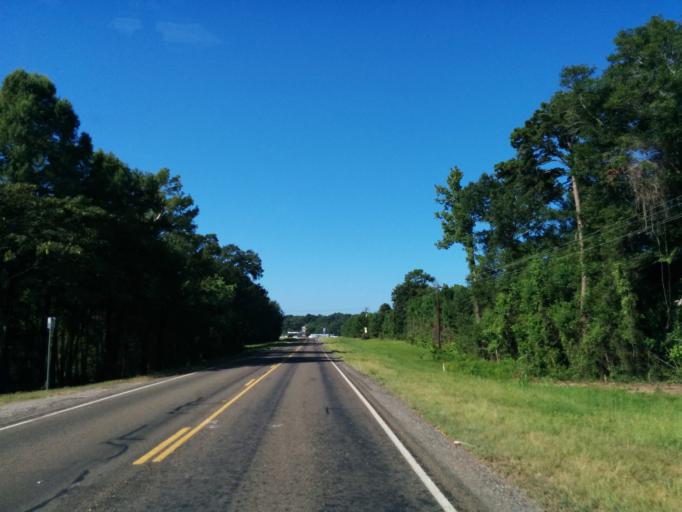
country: US
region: Texas
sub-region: Sabine County
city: Milam
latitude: 31.4533
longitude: -93.7630
